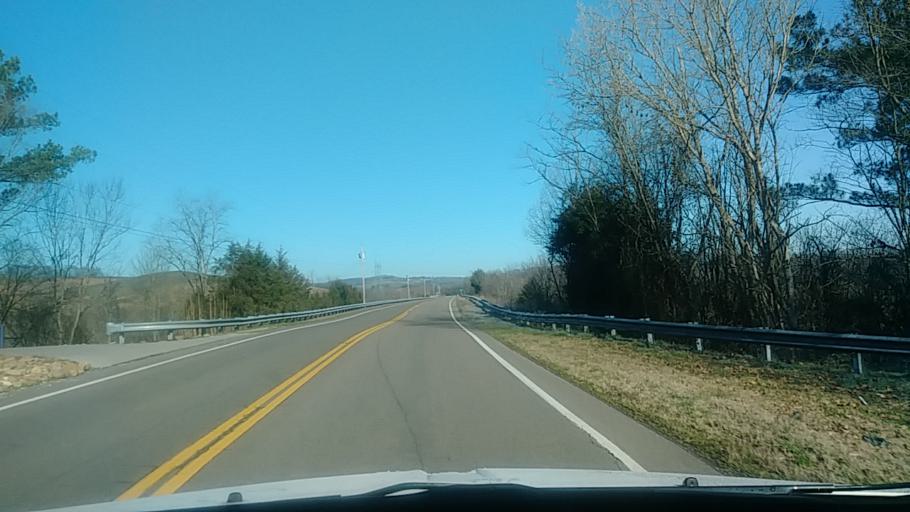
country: US
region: Tennessee
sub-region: Hamblen County
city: Morristown
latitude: 36.1827
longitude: -83.1663
